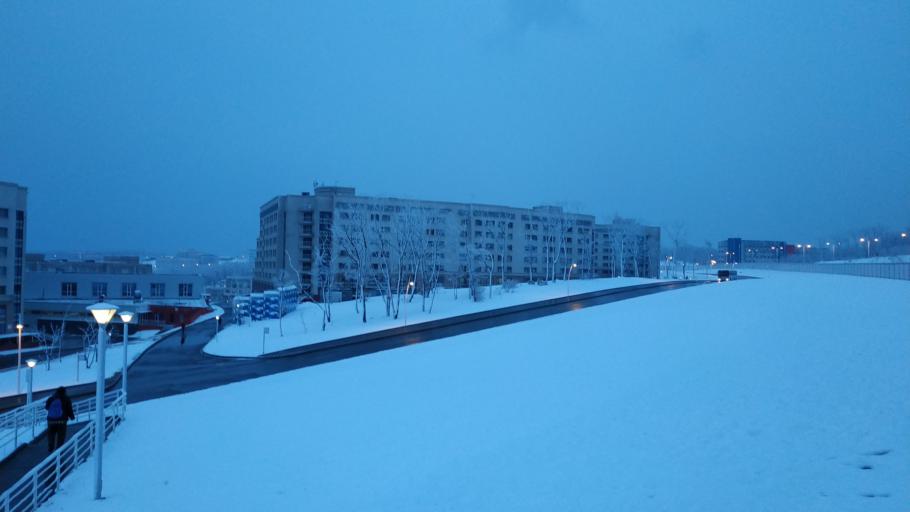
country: RU
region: Primorskiy
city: Russkiy
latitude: 43.0298
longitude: 131.8845
